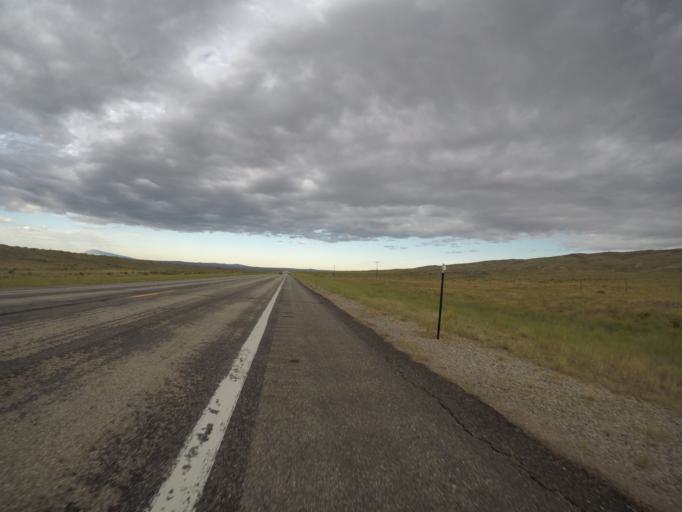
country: US
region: Wyoming
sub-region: Albany County
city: Laramie
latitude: 41.8650
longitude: -106.0885
